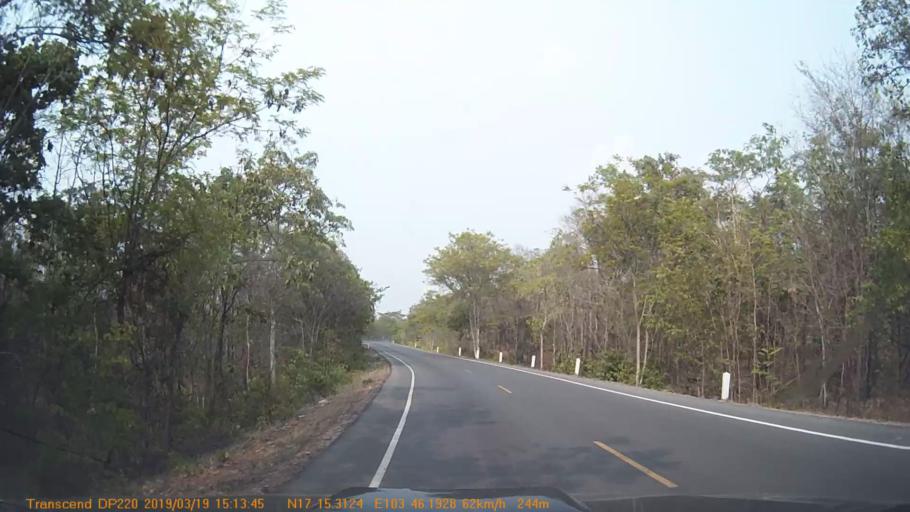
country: TH
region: Sakon Nakhon
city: Nikhom Nam Un
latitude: 17.2555
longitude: 103.7702
